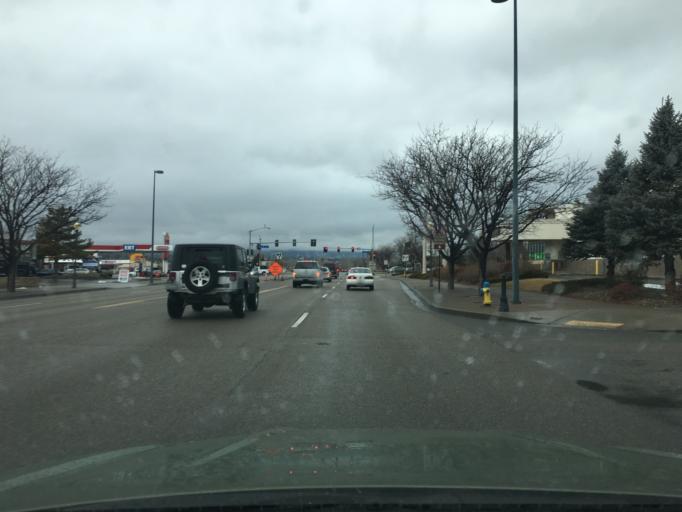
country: US
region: Colorado
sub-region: Mesa County
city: Grand Junction
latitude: 39.0704
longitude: -108.5694
